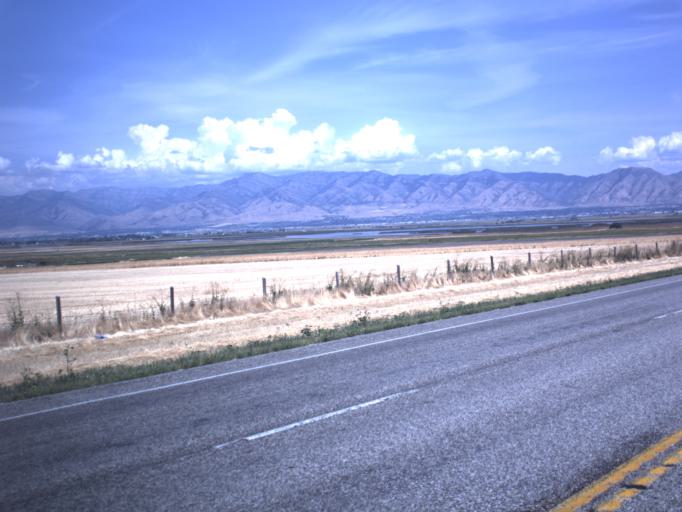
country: US
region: Utah
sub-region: Cache County
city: Mendon
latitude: 41.7530
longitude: -111.9889
